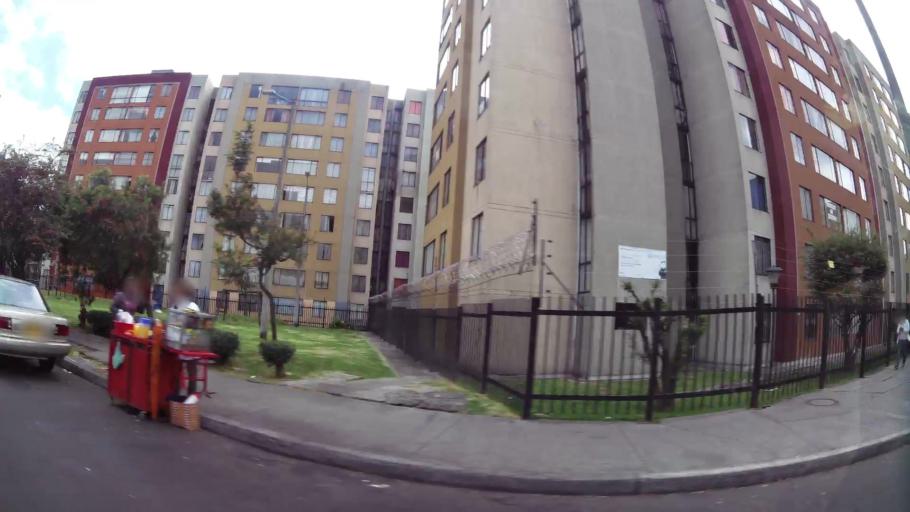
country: CO
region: Bogota D.C.
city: Bogota
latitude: 4.6137
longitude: -74.1092
